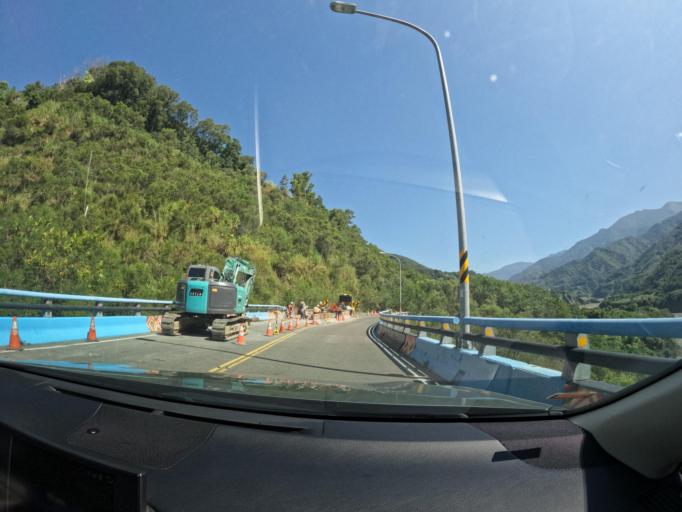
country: TW
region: Taiwan
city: Yujing
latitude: 23.1504
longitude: 120.7569
